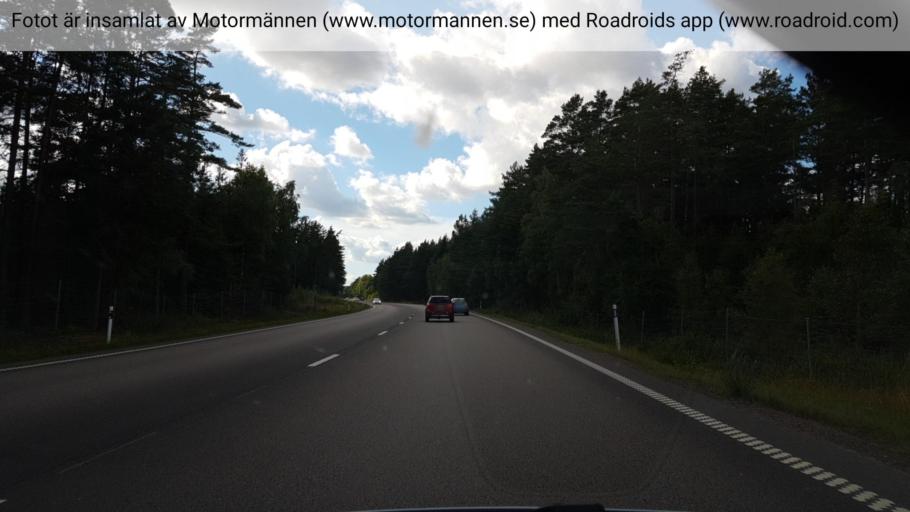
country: SE
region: Vaestra Goetaland
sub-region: Skara Kommun
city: Skara
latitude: 58.4168
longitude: 13.3635
